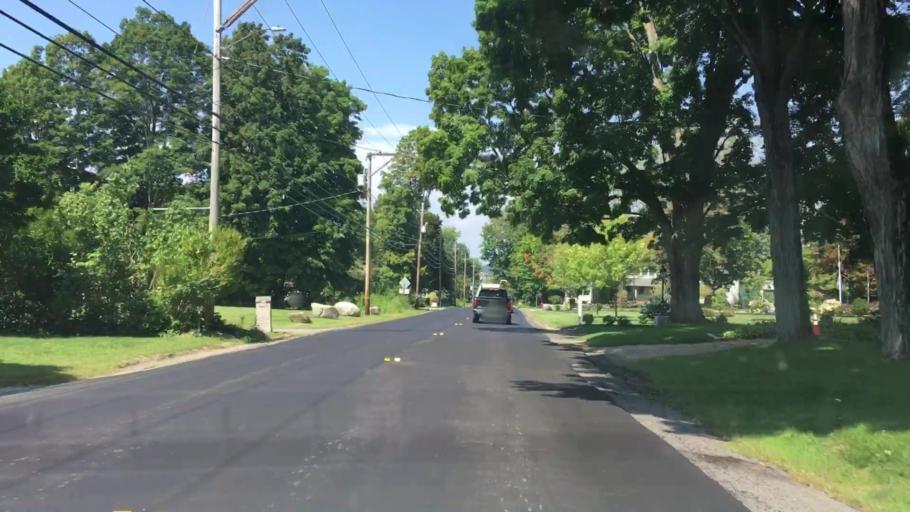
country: US
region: New Hampshire
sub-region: Rockingham County
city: Hampstead
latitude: 42.8794
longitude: -71.1847
